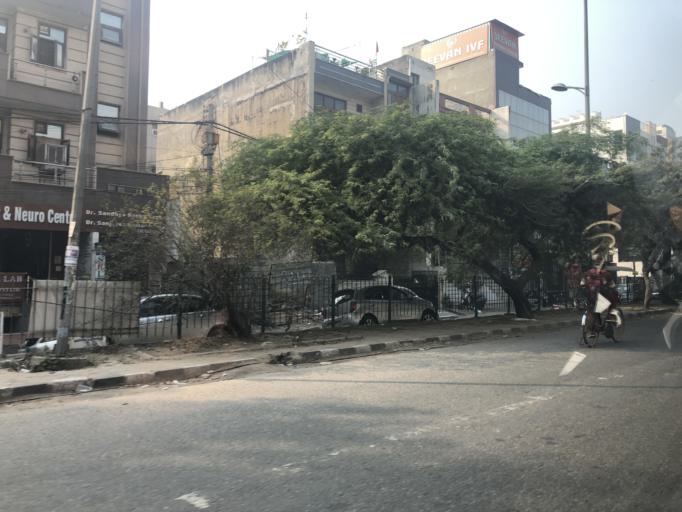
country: IN
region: NCT
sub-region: North West Delhi
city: Pitampura
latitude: 28.6778
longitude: 77.1077
